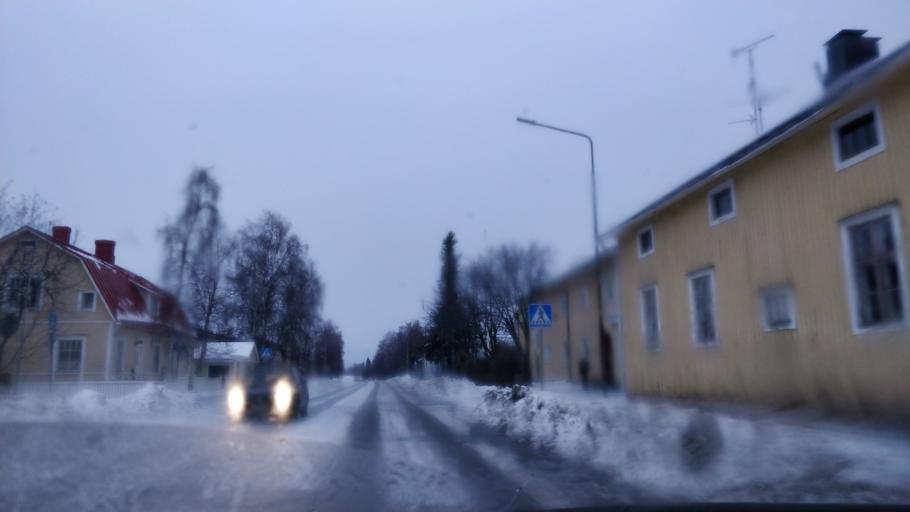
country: FI
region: Lapland
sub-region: Kemi-Tornio
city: Kemi
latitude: 65.7404
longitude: 24.5606
